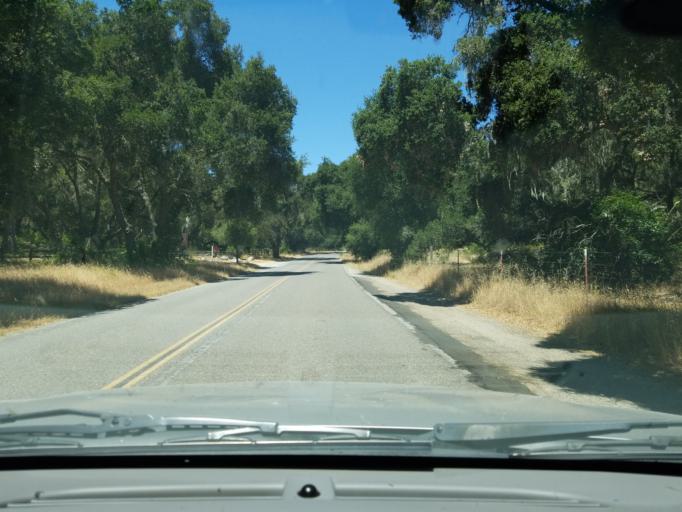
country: US
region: California
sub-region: Monterey County
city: Chualar
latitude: 36.4157
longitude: -121.6038
